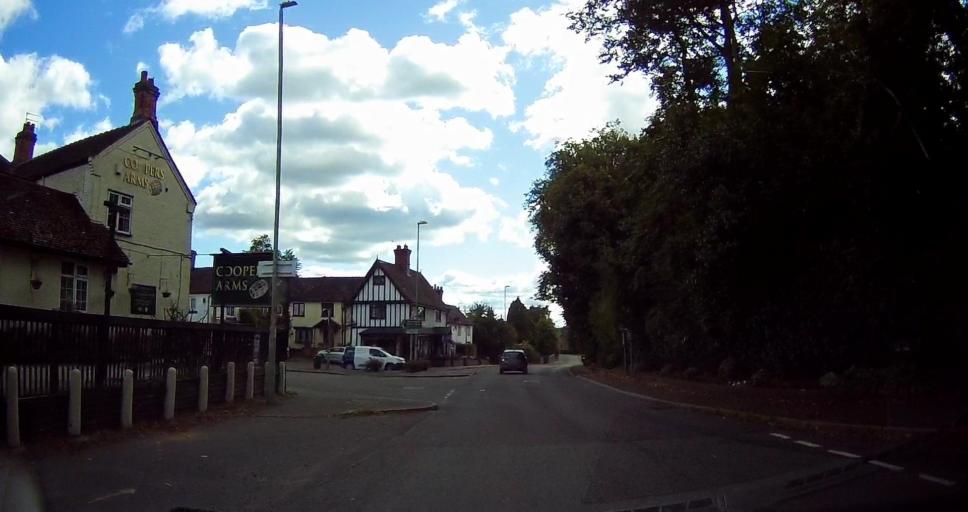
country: GB
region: England
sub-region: Cheshire East
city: Chorlton
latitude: 52.9775
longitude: -2.4029
